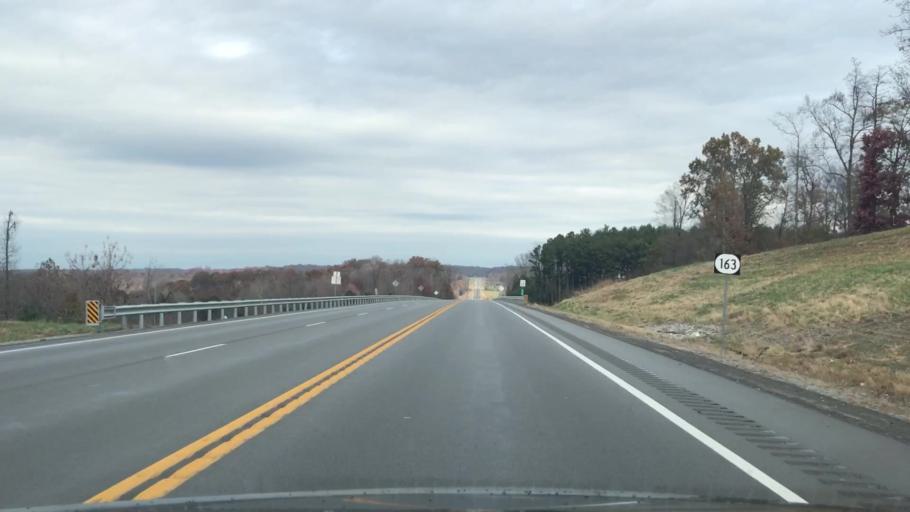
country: US
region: Kentucky
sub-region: Monroe County
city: Tompkinsville
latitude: 36.7915
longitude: -85.6869
